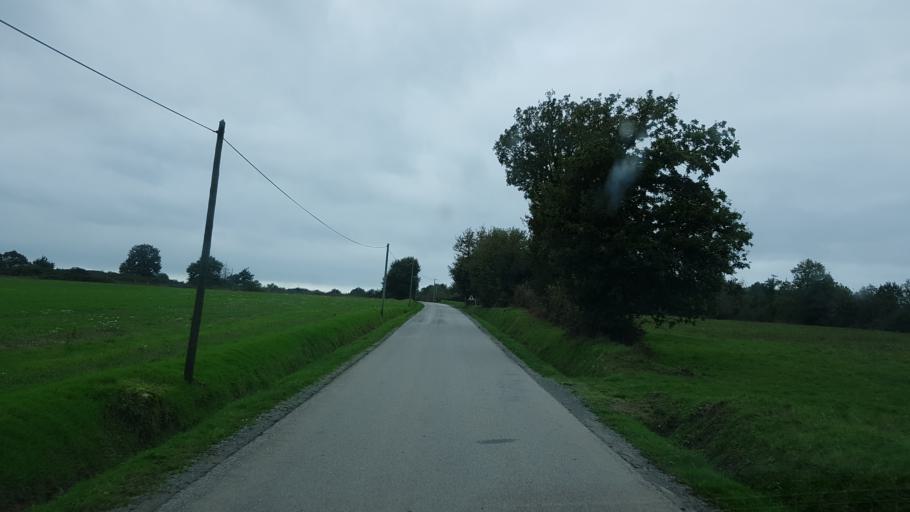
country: FR
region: Brittany
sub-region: Departement du Morbihan
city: Serent
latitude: 47.7810
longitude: -2.4823
